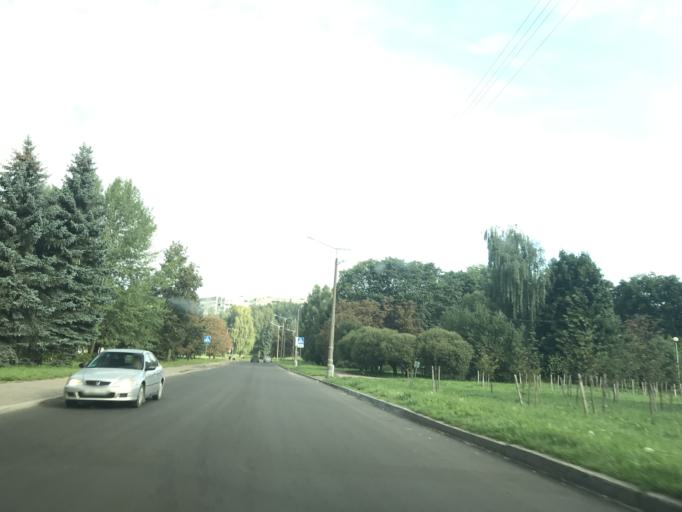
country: BY
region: Minsk
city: Borovlyany
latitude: 53.9479
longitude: 27.6429
